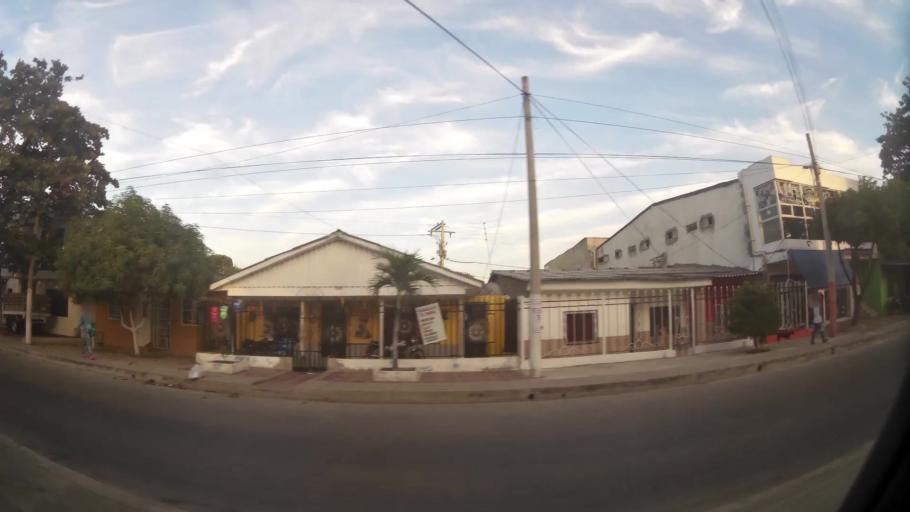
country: CO
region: Atlantico
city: Barranquilla
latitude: 10.9481
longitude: -74.8218
